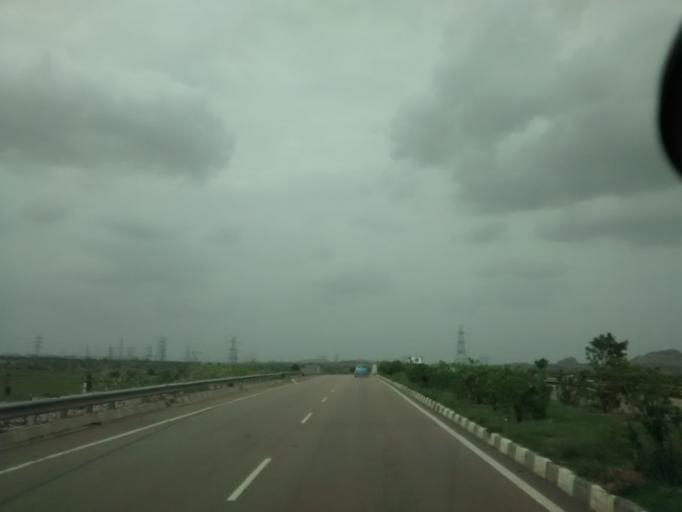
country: IN
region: Andhra Pradesh
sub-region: Kurnool
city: Ramapuram
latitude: 15.1343
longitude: 77.6617
